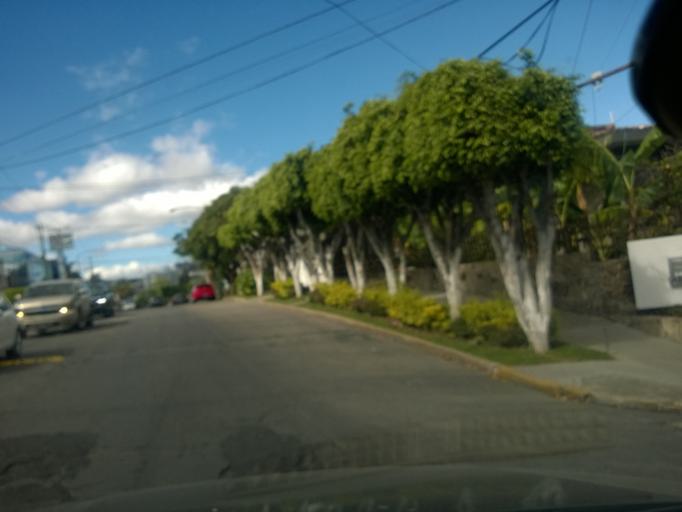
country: MX
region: Guanajuato
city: Leon
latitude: 21.1493
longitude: -101.6953
